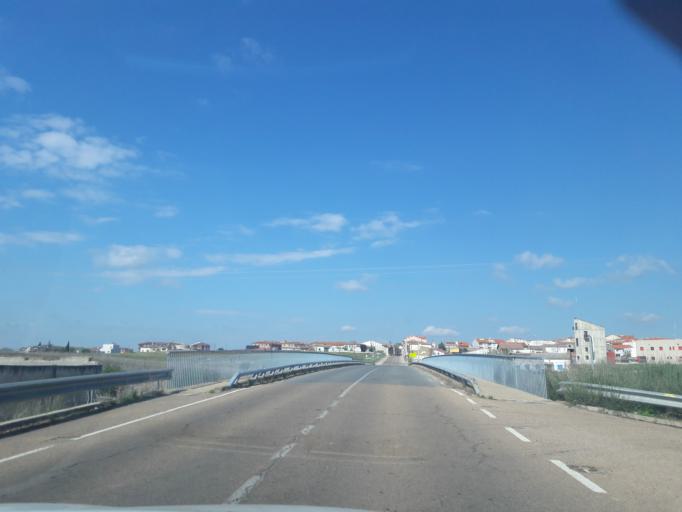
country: ES
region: Castille and Leon
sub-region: Provincia de Salamanca
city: Ciudad Rodrigo
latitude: 40.5947
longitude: -6.5181
